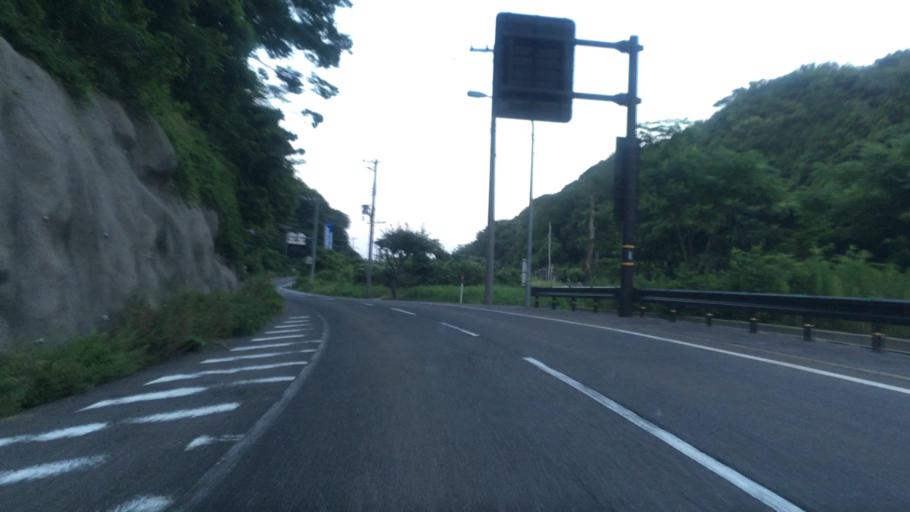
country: JP
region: Tottori
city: Tottori
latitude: 35.6152
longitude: 134.3934
